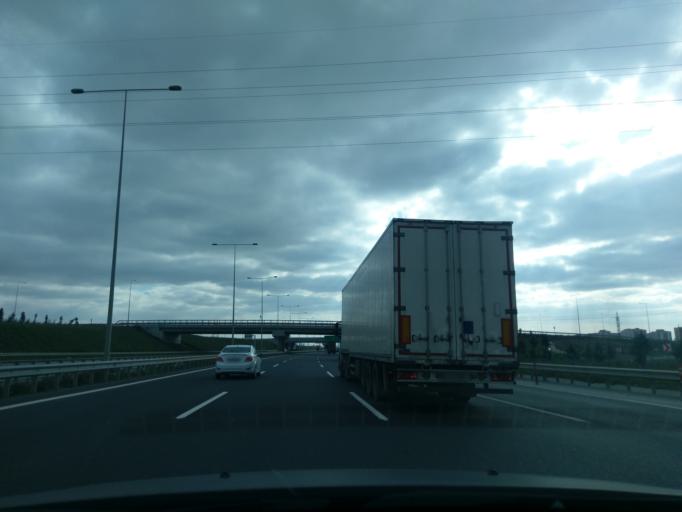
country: TR
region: Istanbul
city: Basaksehir
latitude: 41.1195
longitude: 28.8142
